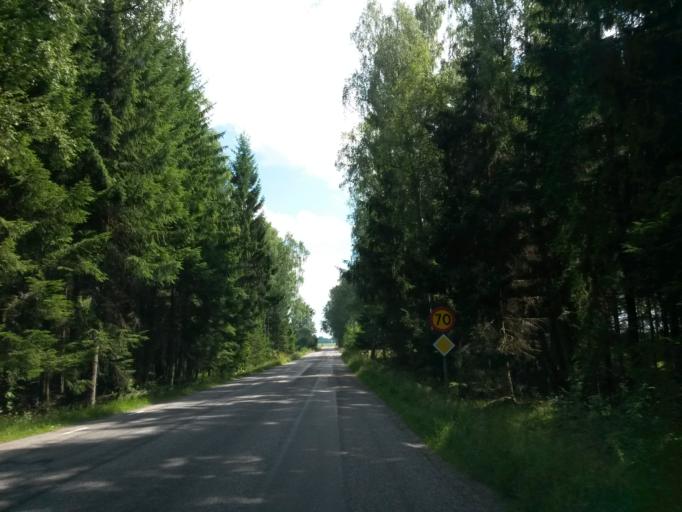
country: SE
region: Vaestra Goetaland
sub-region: Essunga Kommun
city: Nossebro
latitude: 58.1532
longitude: 12.7506
